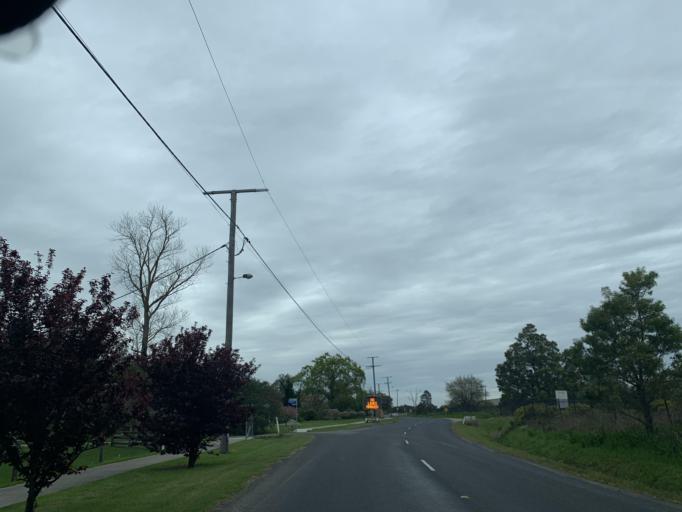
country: AU
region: Victoria
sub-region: Cardinia
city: Garfield
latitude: -38.0853
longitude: 145.6268
